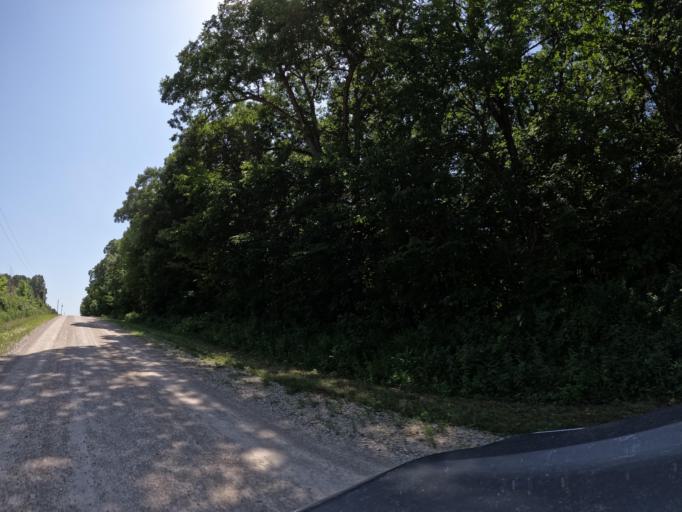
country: US
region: Iowa
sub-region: Henry County
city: Mount Pleasant
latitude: 40.9928
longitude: -91.6363
